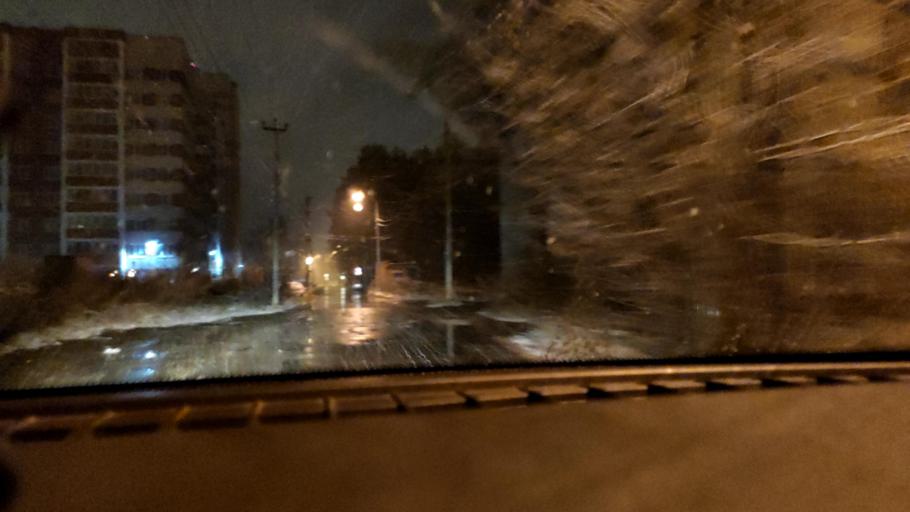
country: RU
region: Perm
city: Perm
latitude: 57.9942
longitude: 56.1795
